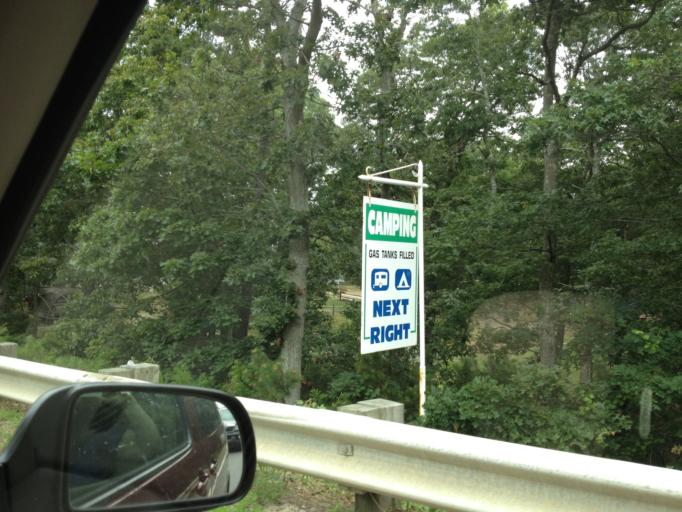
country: US
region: Massachusetts
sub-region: Barnstable County
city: Eastham
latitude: 41.8448
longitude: -69.9842
